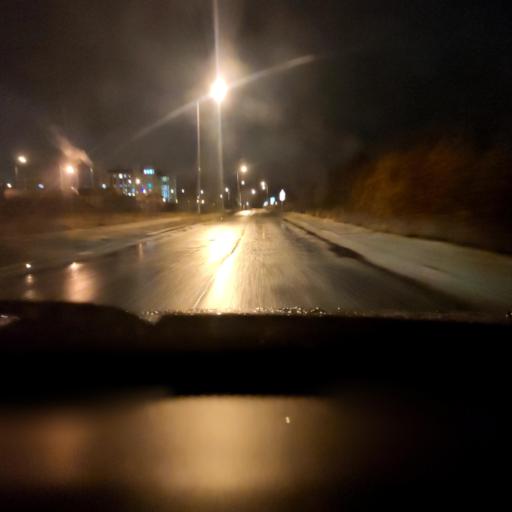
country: RU
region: Perm
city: Perm
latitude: 58.0373
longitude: 56.1809
